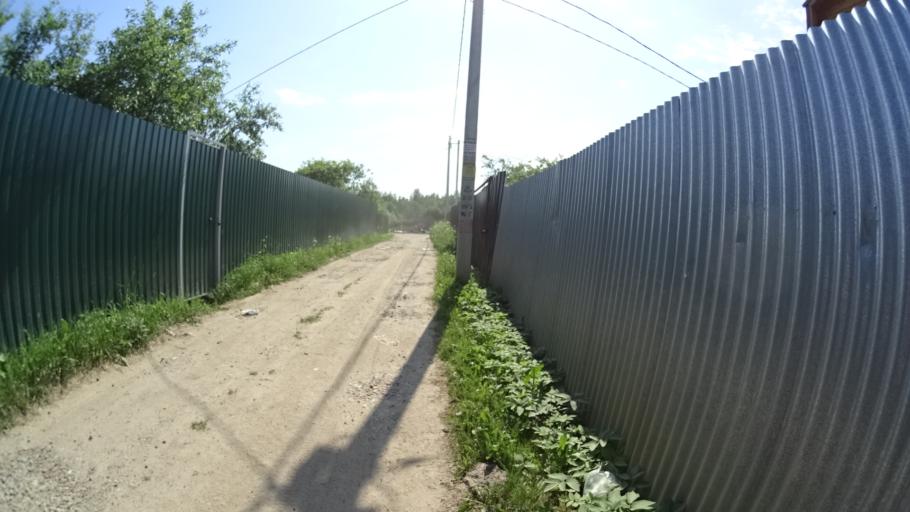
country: RU
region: Moskovskaya
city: Zelenogradskiy
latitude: 56.0836
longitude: 37.9366
